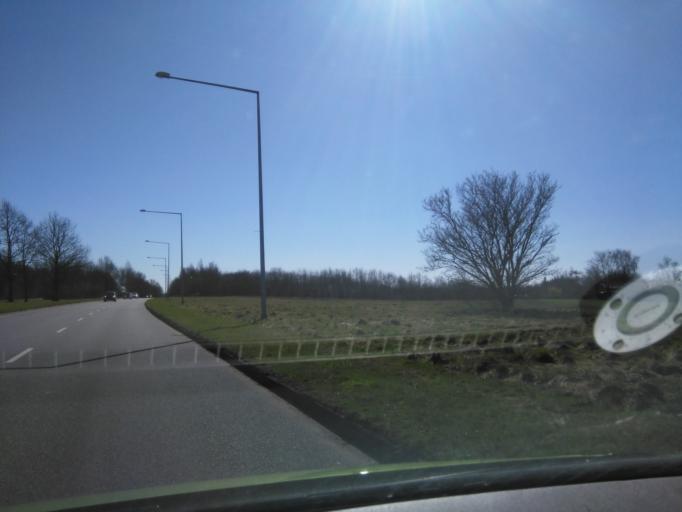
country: DK
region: Central Jutland
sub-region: Arhus Kommune
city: Lystrup
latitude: 56.2458
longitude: 10.2339
